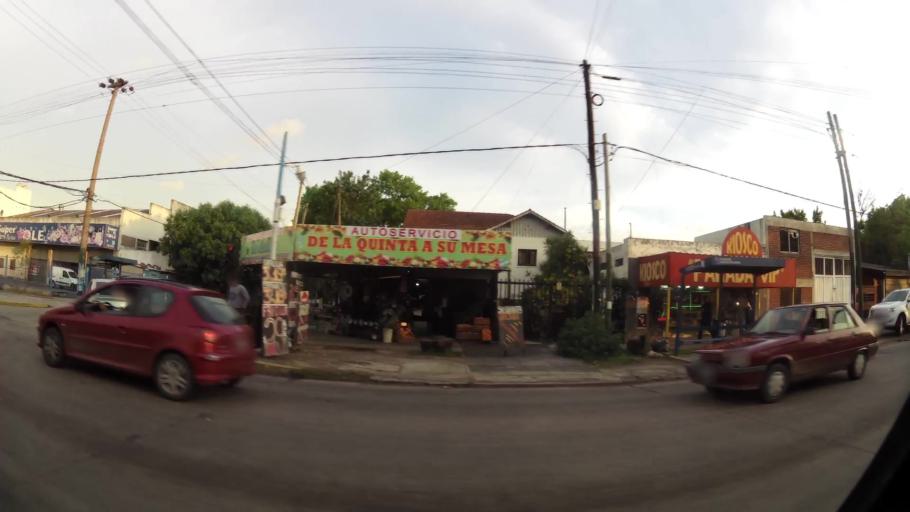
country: AR
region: Buenos Aires
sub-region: Partido de Lomas de Zamora
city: Lomas de Zamora
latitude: -34.7683
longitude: -58.3753
